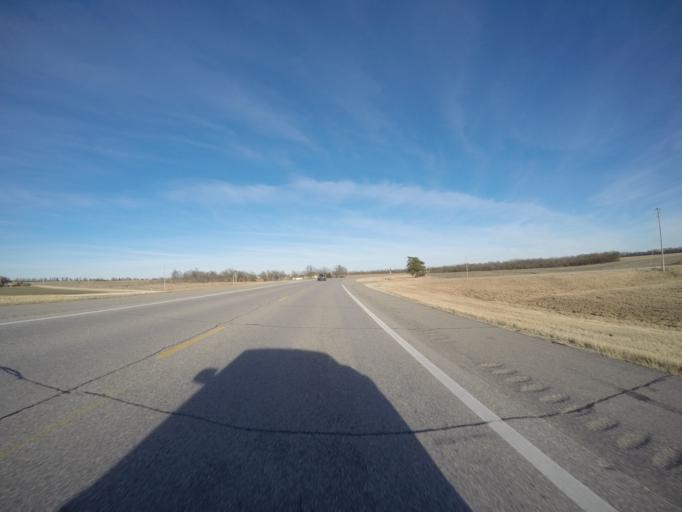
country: US
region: Kansas
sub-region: Marion County
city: Peabody
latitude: 38.1740
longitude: -97.1906
